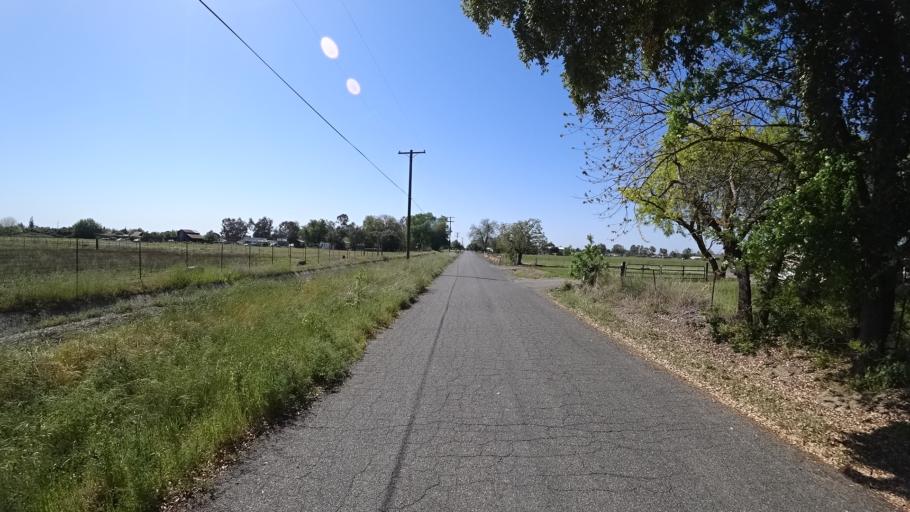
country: US
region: California
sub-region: Glenn County
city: Orland
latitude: 39.7314
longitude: -122.1829
